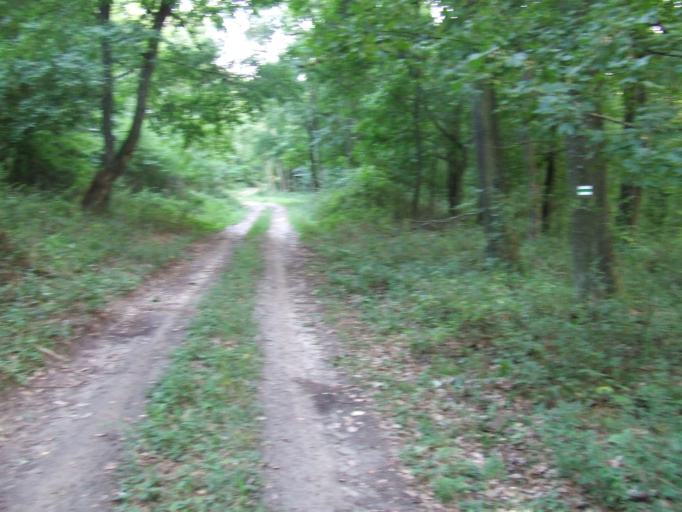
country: HU
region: Somogy
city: Kethely
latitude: 46.6383
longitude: 17.3389
